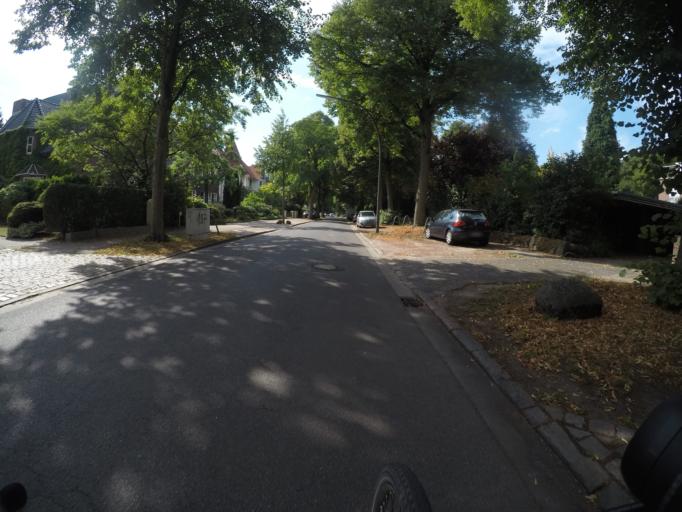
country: DE
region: Hamburg
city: Marienthal
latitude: 53.5664
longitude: 10.0875
